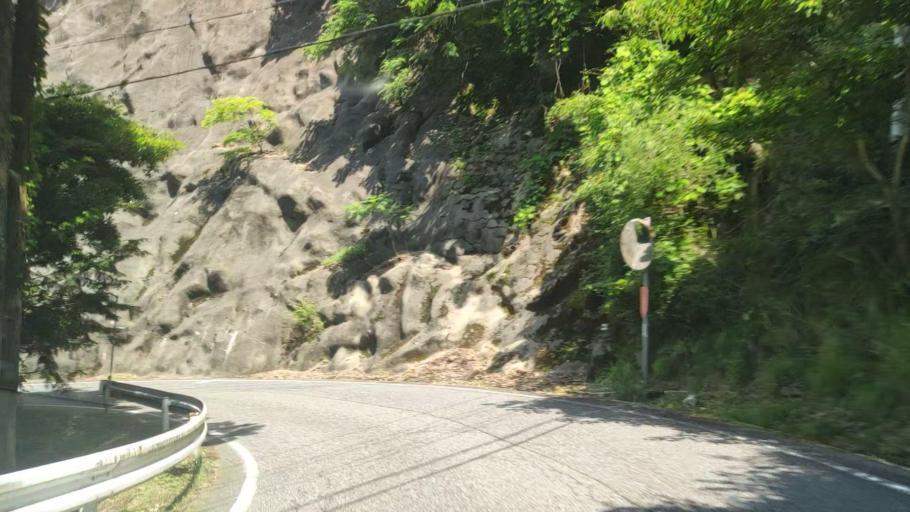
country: JP
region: Hyogo
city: Toyooka
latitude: 35.6385
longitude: 134.7706
